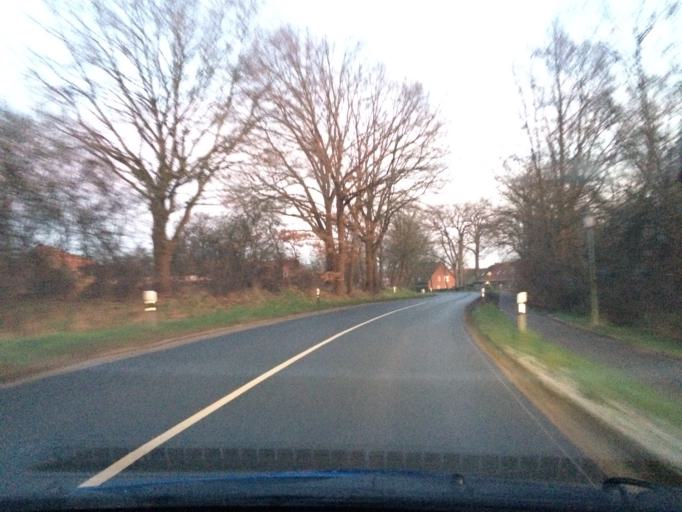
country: DE
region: Lower Saxony
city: Melbeck
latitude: 53.1813
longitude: 10.4018
